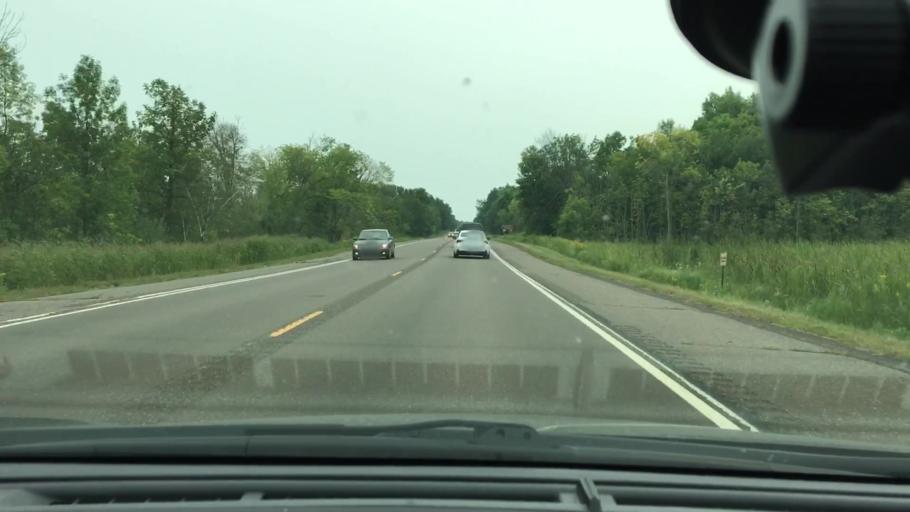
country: US
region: Minnesota
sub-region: Mille Lacs County
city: Vineland
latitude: 46.1489
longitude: -93.7366
